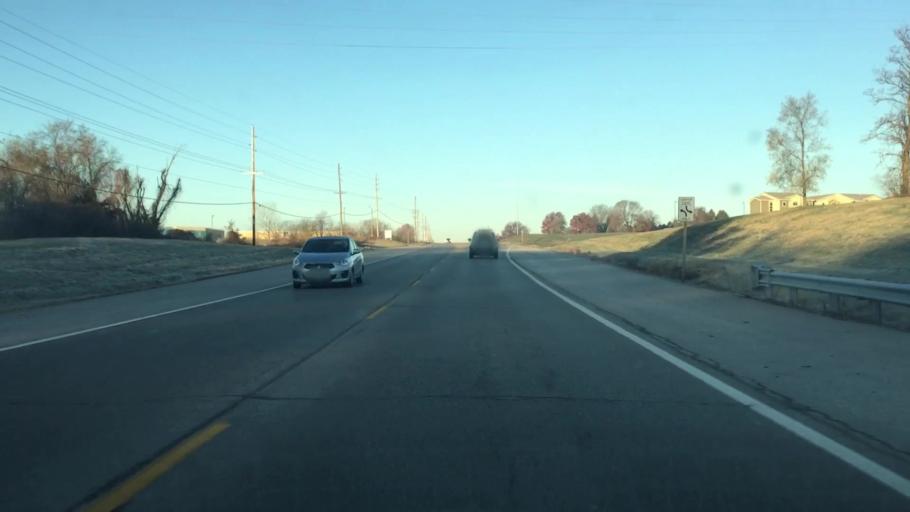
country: US
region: Missouri
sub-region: Buchanan County
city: Saint Joseph
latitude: 39.7555
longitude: -94.7750
